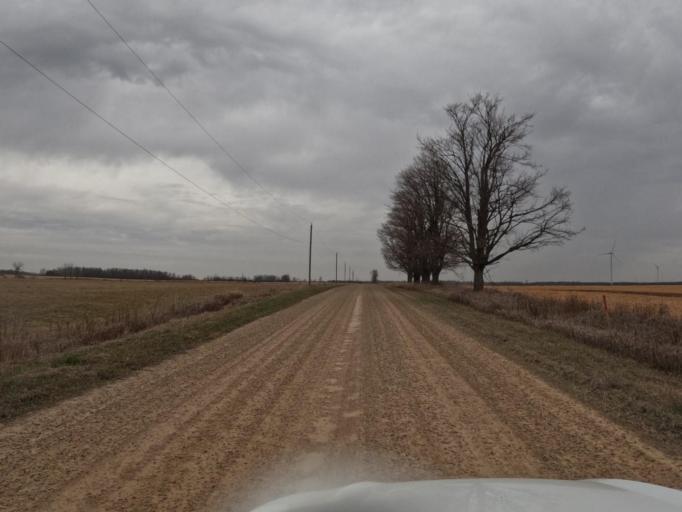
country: CA
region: Ontario
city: Shelburne
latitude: 43.8819
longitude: -80.3812
